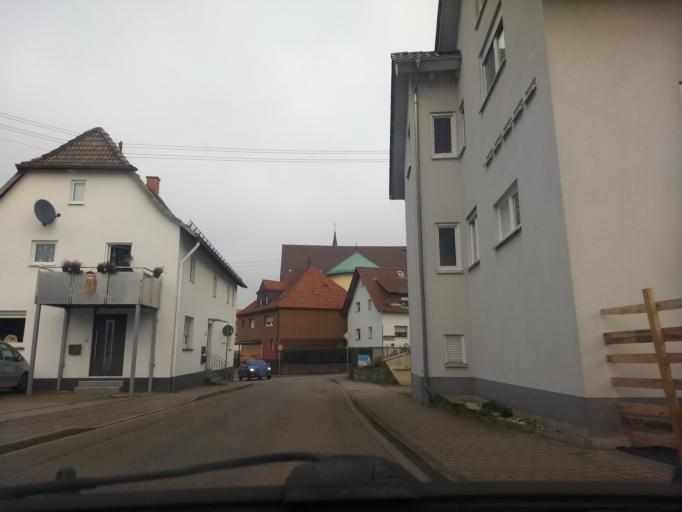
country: DE
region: Baden-Wuerttemberg
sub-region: Karlsruhe Region
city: Kuppenheim
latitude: 48.8045
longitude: 8.2216
